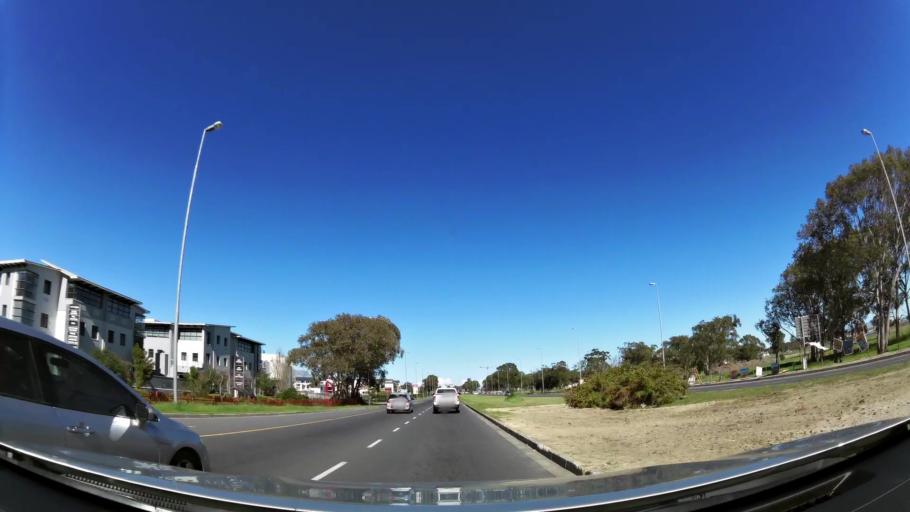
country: ZA
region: Western Cape
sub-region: Cape Winelands District Municipality
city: Stellenbosch
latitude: -34.0866
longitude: 18.8201
